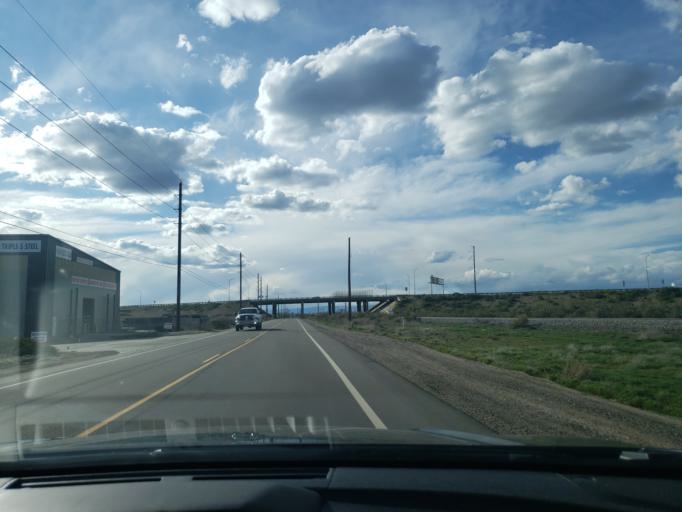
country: US
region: Colorado
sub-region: Mesa County
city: Redlands
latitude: 39.1095
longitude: -108.6451
